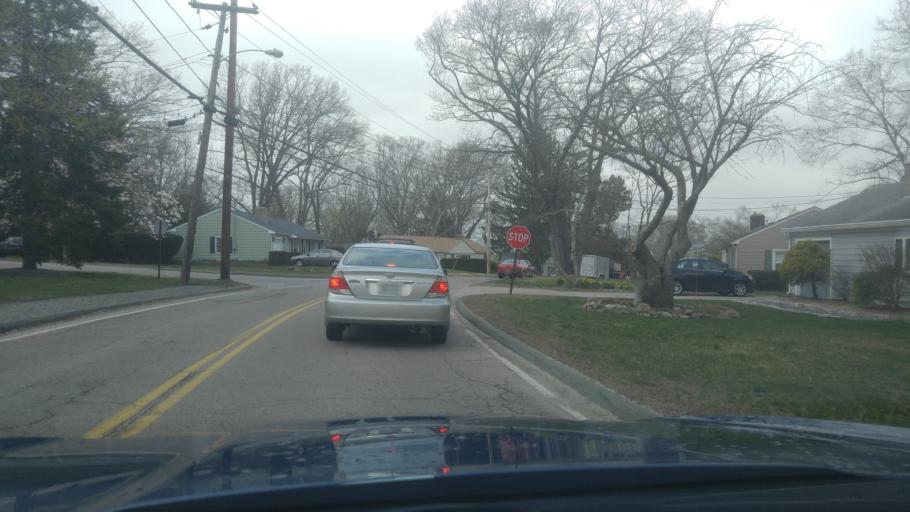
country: US
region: Rhode Island
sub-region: Kent County
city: East Greenwich
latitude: 41.6918
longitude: -71.4715
